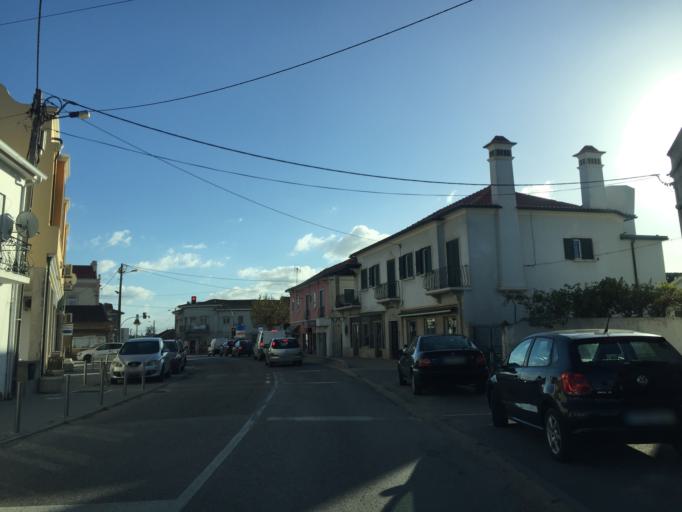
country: PT
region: Leiria
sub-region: Leiria
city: Monte Redondo
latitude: 39.9476
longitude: -8.7845
